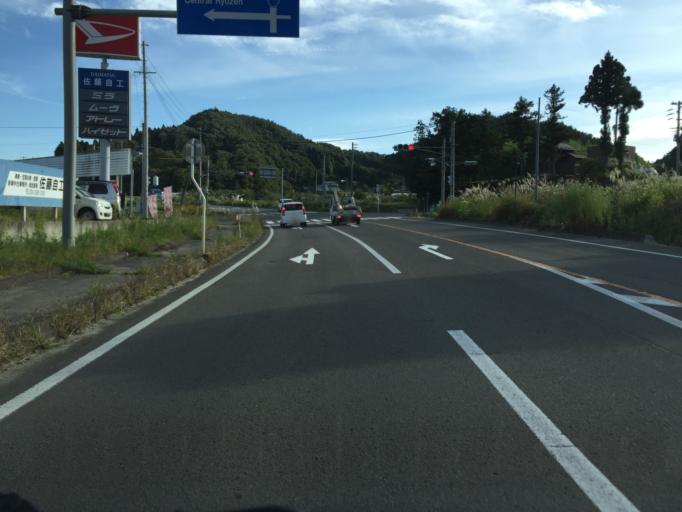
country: JP
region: Fukushima
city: Hobaramachi
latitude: 37.7800
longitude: 140.5901
